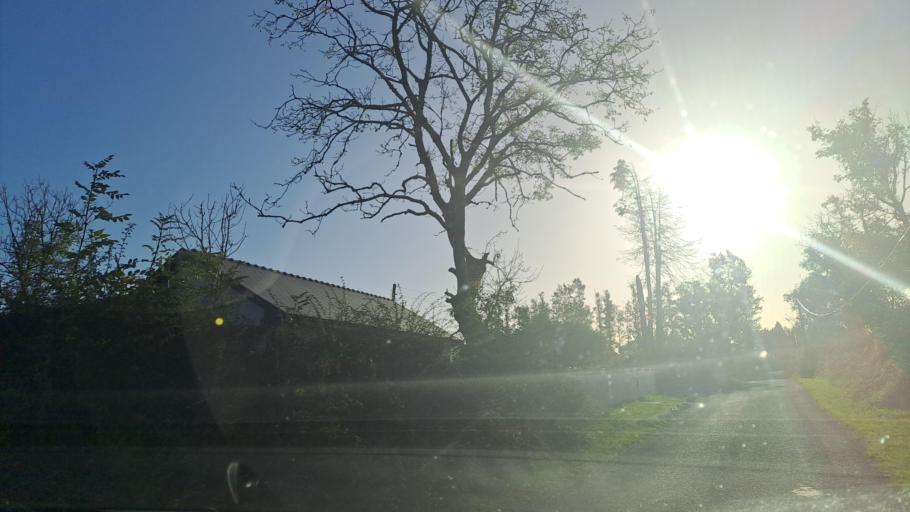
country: IE
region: Ulster
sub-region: An Cabhan
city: Kingscourt
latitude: 53.9815
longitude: -6.8546
